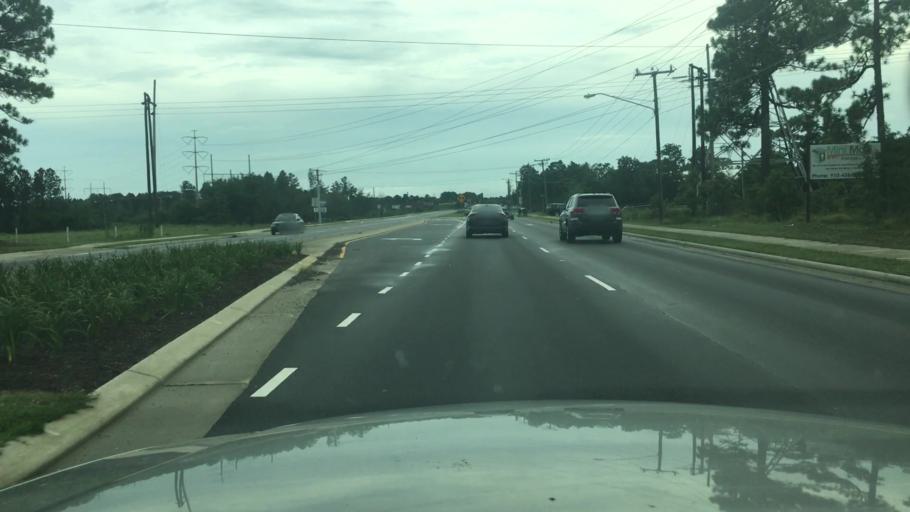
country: US
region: North Carolina
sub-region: Cumberland County
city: Hope Mills
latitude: 35.0099
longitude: -78.9110
